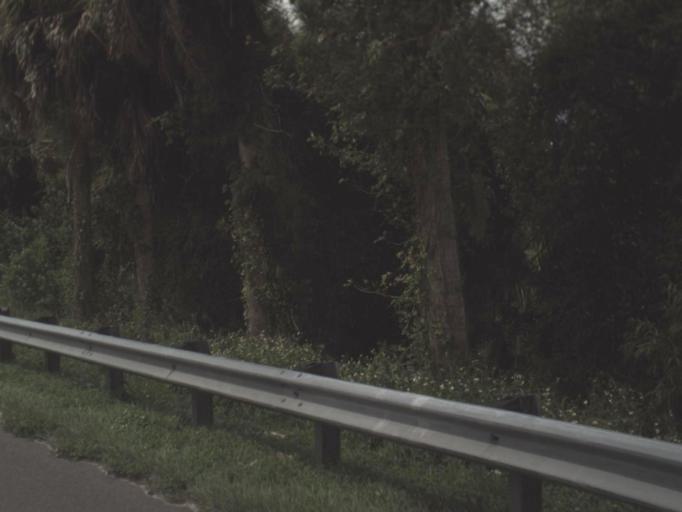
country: US
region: Florida
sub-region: Glades County
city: Buckhead Ridge
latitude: 27.2249
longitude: -81.0958
